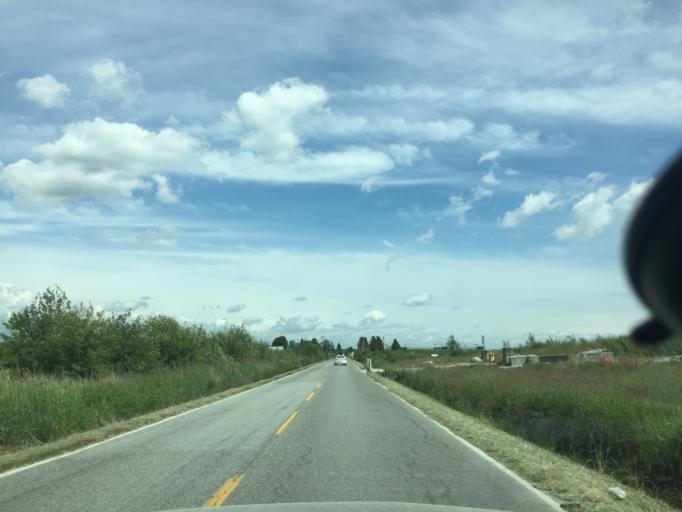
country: CA
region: British Columbia
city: Richmond
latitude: 49.2067
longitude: -123.1831
